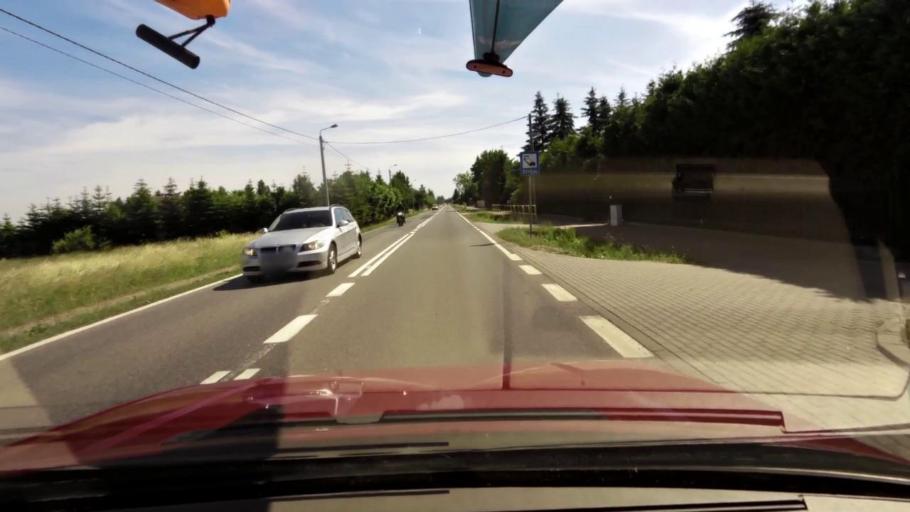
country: PL
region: Pomeranian Voivodeship
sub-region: Powiat slupski
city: Kobylnica
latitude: 54.4227
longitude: 17.0073
